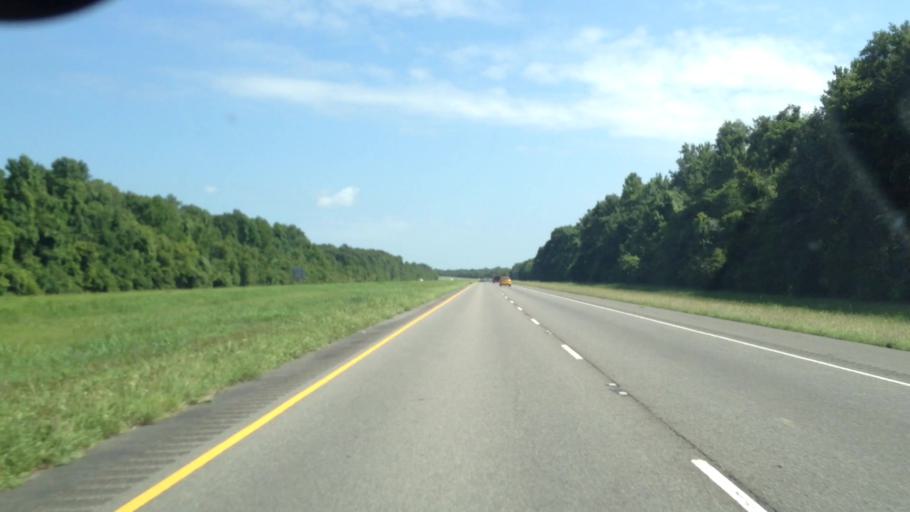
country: US
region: Louisiana
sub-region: Avoyelles Parish
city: Bunkie
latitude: 30.8834
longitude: -92.2270
